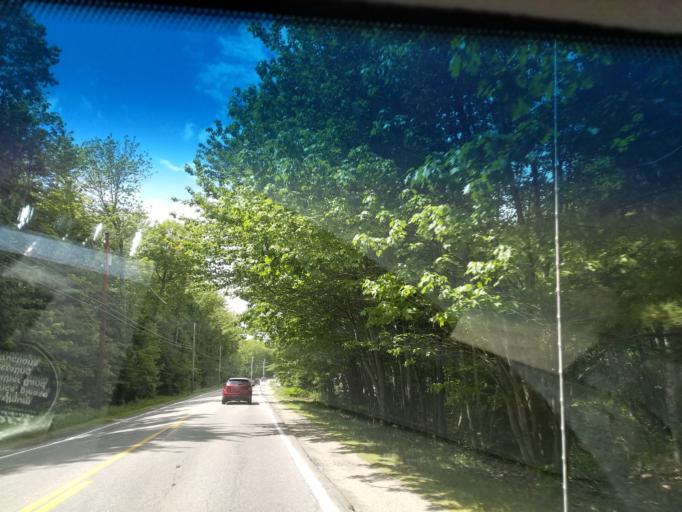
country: US
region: Maine
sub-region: Cumberland County
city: Westbrook
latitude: 43.6289
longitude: -70.3768
